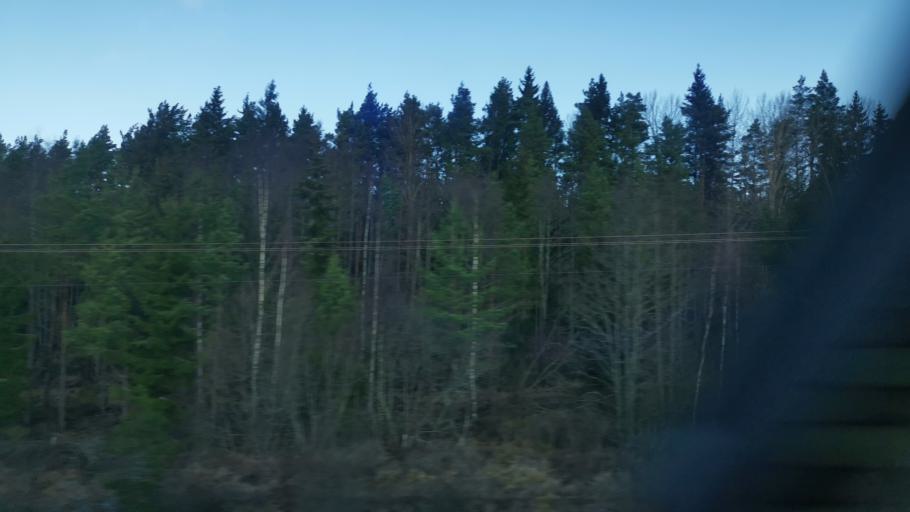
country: SE
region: Soedermanland
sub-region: Flens Kommun
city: Malmkoping
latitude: 59.0680
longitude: 16.7638
